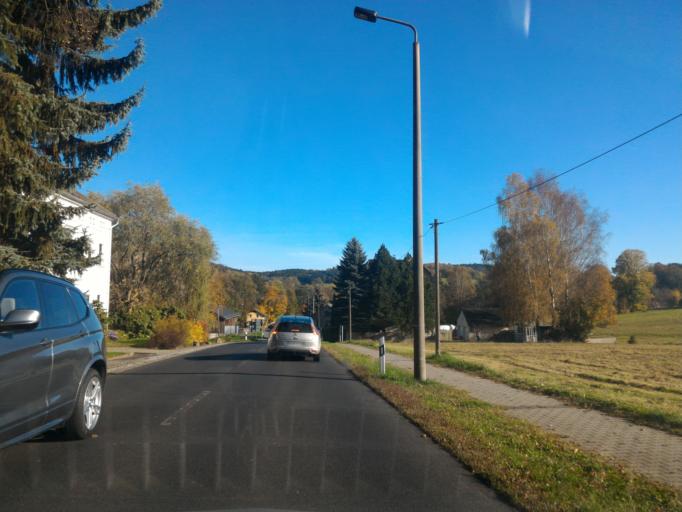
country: DE
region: Saxony
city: Sohland
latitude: 51.0341
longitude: 14.4458
